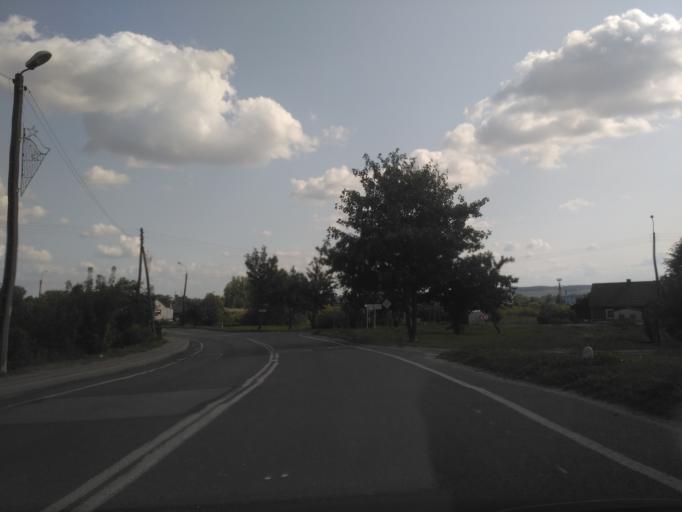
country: PL
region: Lublin Voivodeship
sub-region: Powiat chelmski
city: Rejowiec Fabryczny
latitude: 51.1150
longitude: 23.2463
